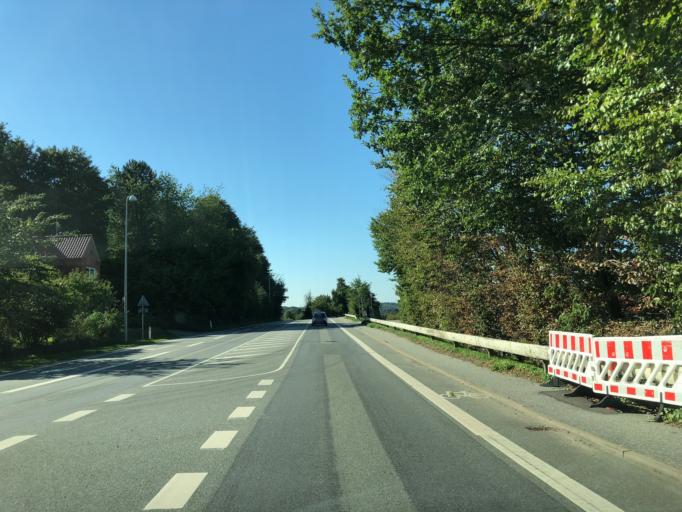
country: DK
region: South Denmark
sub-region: Aabenraa Kommune
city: Aabenraa
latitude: 55.0158
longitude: 9.4614
